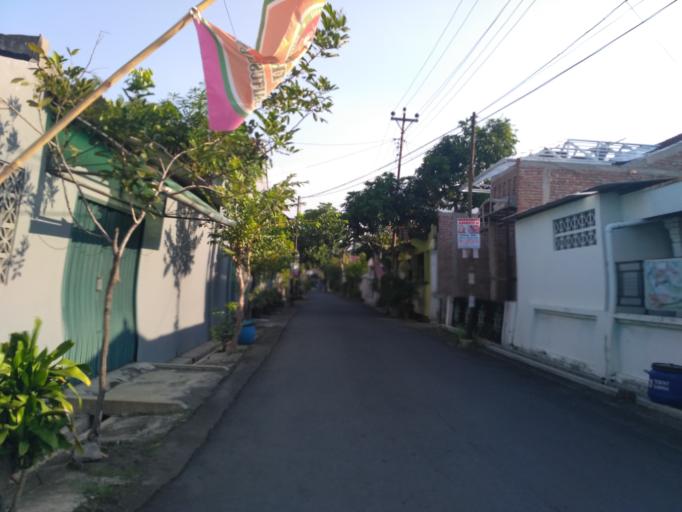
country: ID
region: Central Java
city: Mranggen
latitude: -7.0226
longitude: 110.4652
